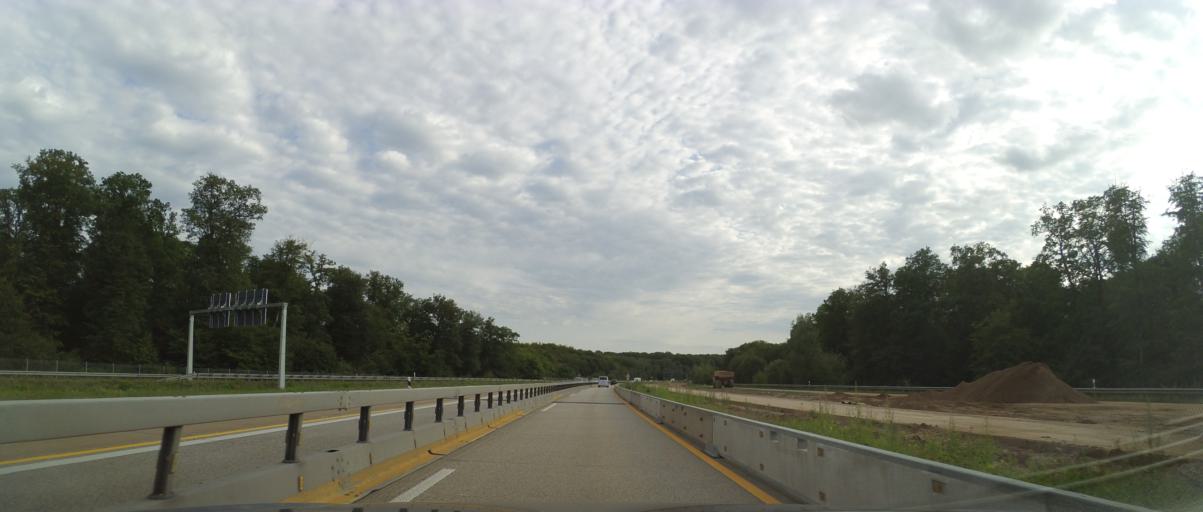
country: DE
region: Rheinland-Pfalz
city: Altrich
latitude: 49.9455
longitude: 6.8827
